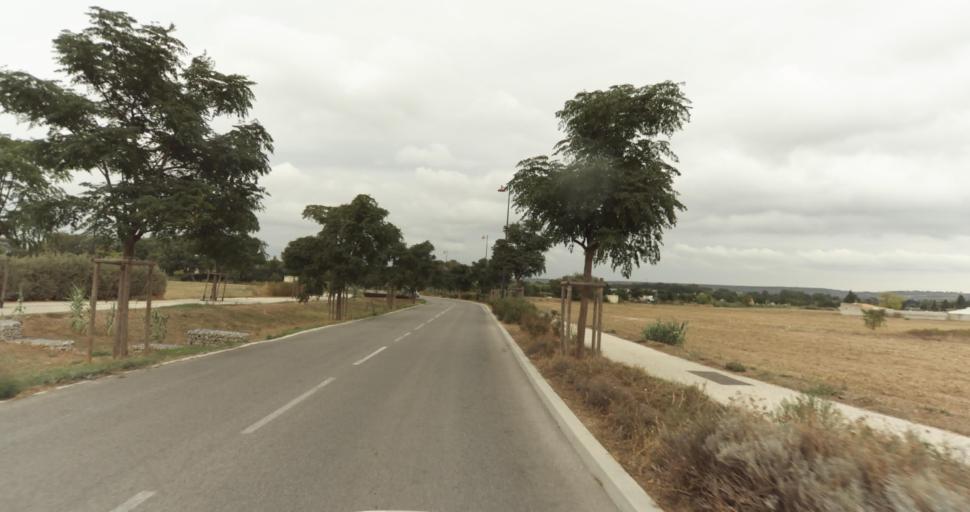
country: FR
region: Provence-Alpes-Cote d'Azur
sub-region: Departement des Bouches-du-Rhone
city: Saint-Victoret
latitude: 43.4124
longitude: 5.2564
